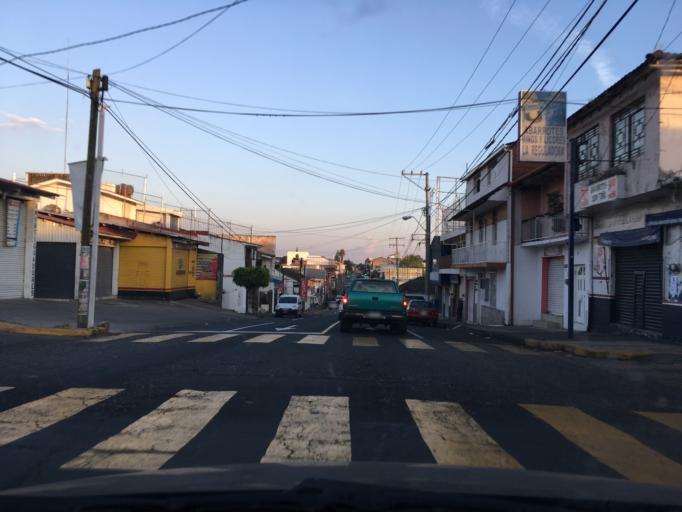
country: MX
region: Michoacan
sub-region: Uruapan
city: Uruapan
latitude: 19.4158
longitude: -102.0610
